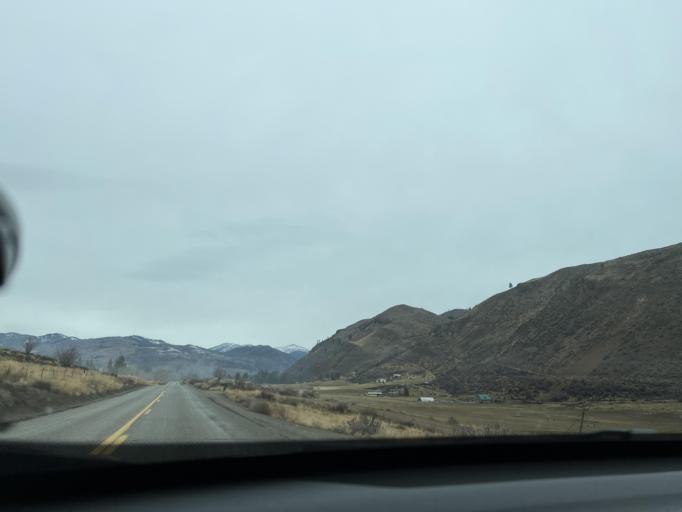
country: US
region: Washington
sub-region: Okanogan County
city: Brewster
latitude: 48.5170
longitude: -120.1761
